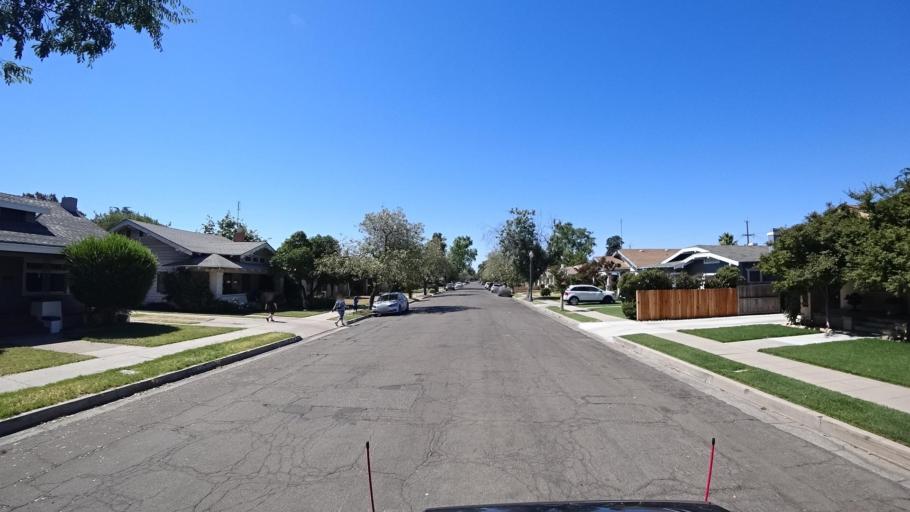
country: US
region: California
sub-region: Fresno County
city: Fresno
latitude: 36.7610
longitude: -119.8069
